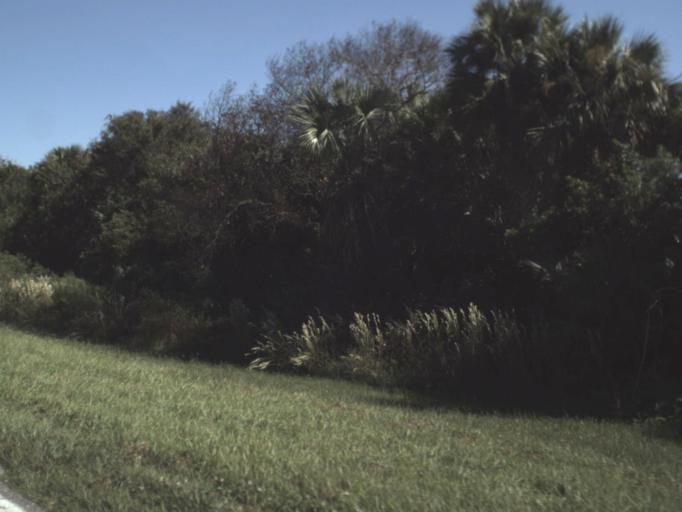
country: US
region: Florida
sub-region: Hendry County
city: Port LaBelle
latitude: 26.7684
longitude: -81.2775
